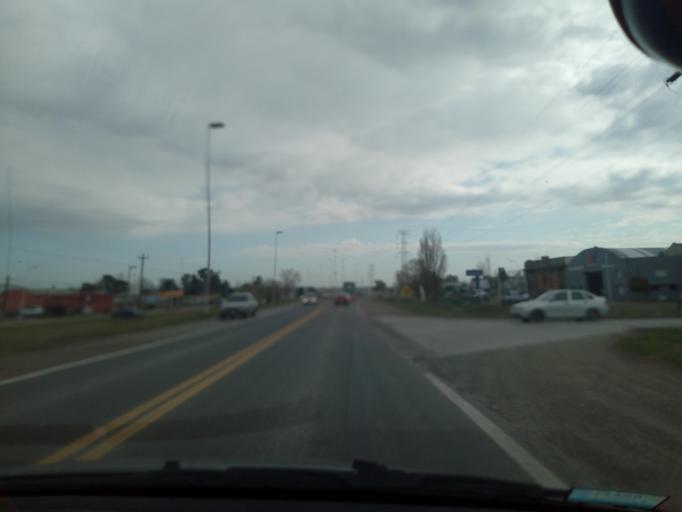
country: AR
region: Buenos Aires
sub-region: Partido de Tandil
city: Tandil
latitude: -37.3209
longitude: -59.1021
